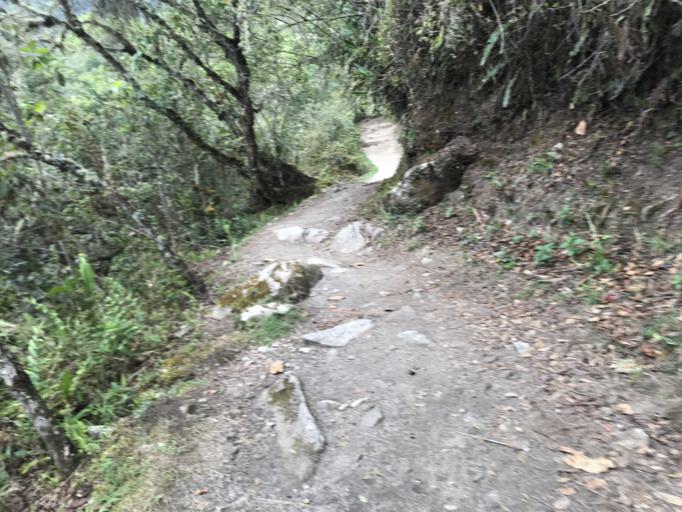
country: PE
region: Cusco
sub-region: Provincia de La Convencion
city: Santa Teresa
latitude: -13.1871
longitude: -72.5385
